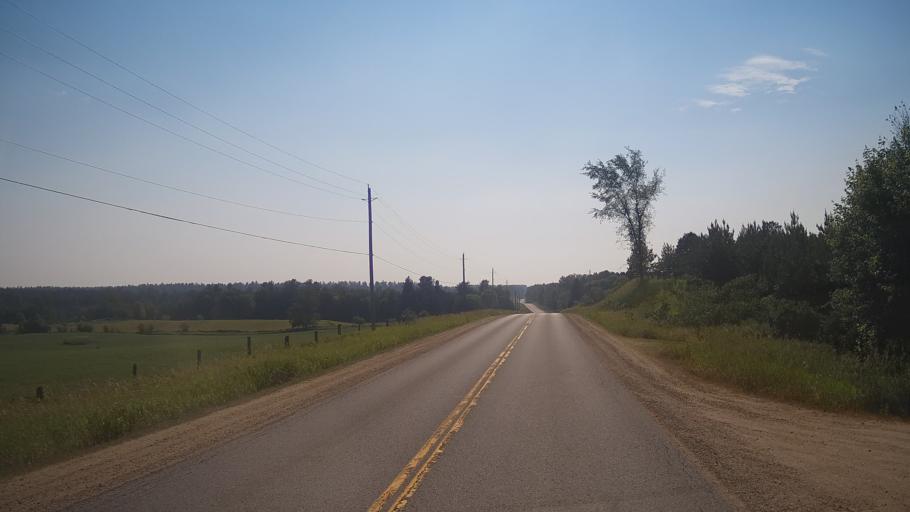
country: CA
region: Ontario
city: Pembroke
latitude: 45.6129
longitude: -77.1941
